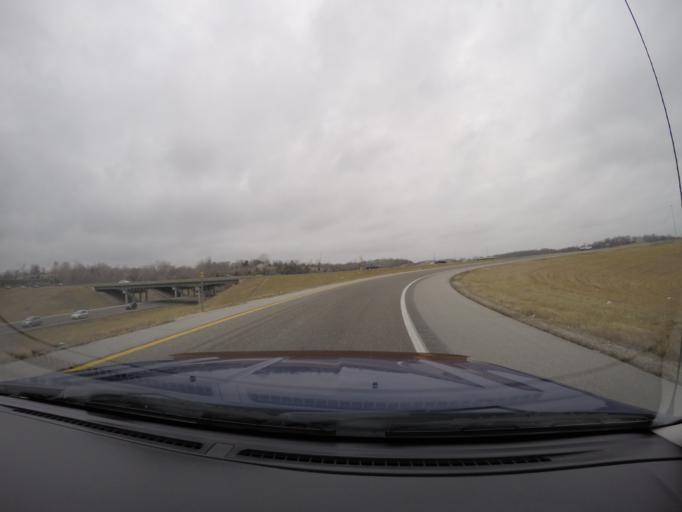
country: US
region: Kansas
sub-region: Wyandotte County
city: Edwardsville
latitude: 39.1047
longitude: -94.8095
